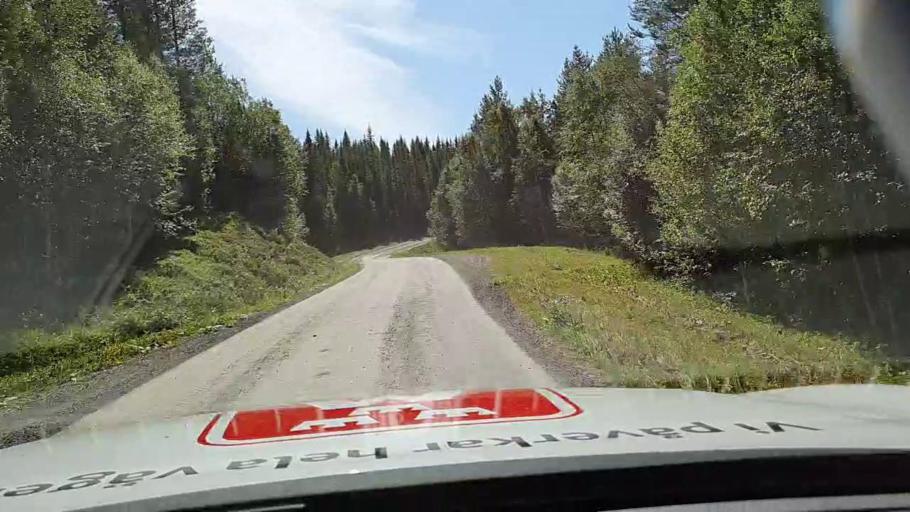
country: SE
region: Jaemtland
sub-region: Krokoms Kommun
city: Valla
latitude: 64.1029
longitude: 14.1508
